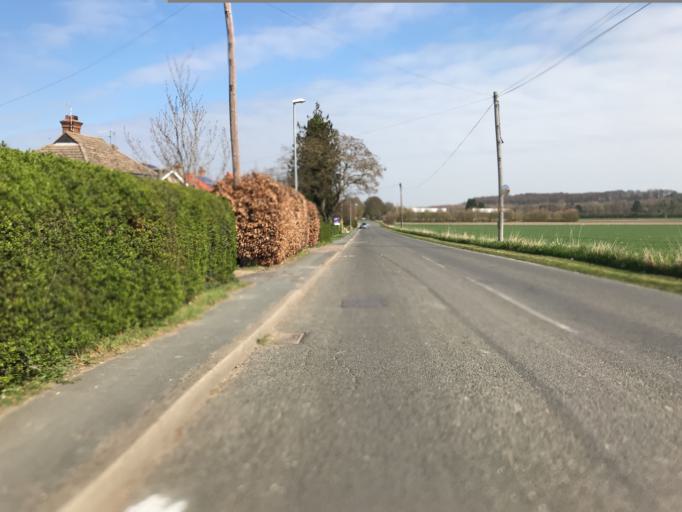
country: GB
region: England
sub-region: Cambridgeshire
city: Sawston
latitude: 52.1613
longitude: 0.1575
